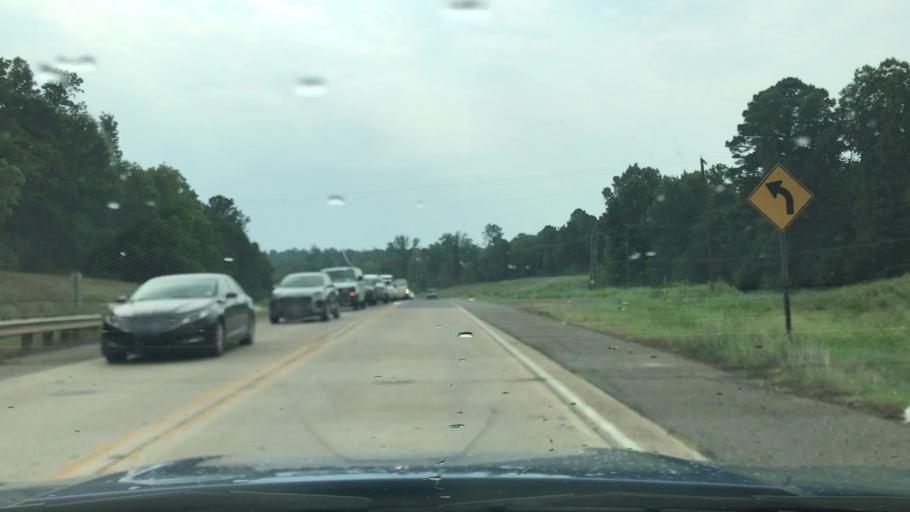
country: US
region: Louisiana
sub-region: Caddo Parish
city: Greenwood
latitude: 32.4525
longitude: -94.0118
